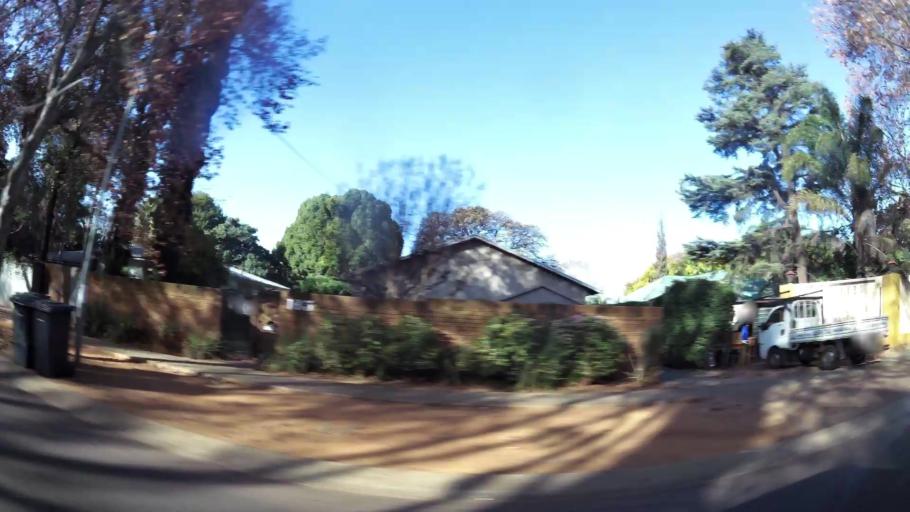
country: ZA
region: Gauteng
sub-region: City of Tshwane Metropolitan Municipality
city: Pretoria
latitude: -25.7309
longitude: 28.2150
